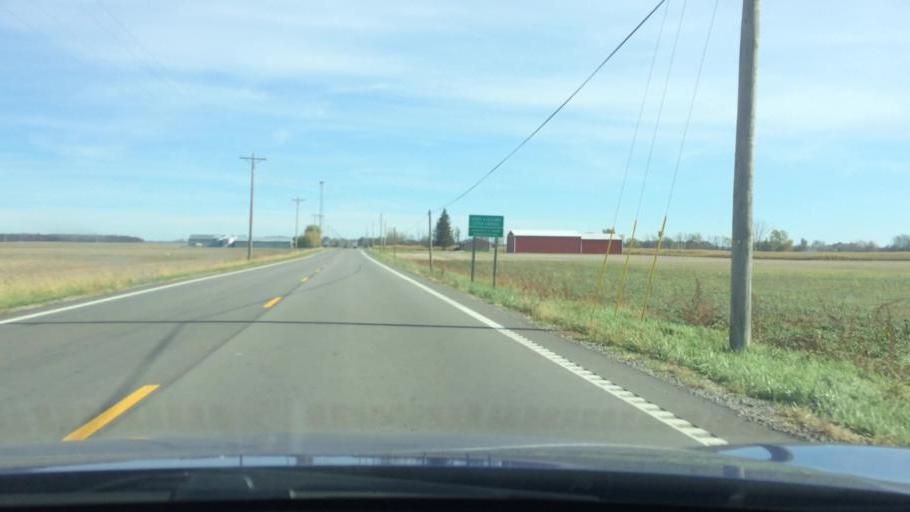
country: US
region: Ohio
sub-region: Logan County
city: Russells Point
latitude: 40.4394
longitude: -83.9009
